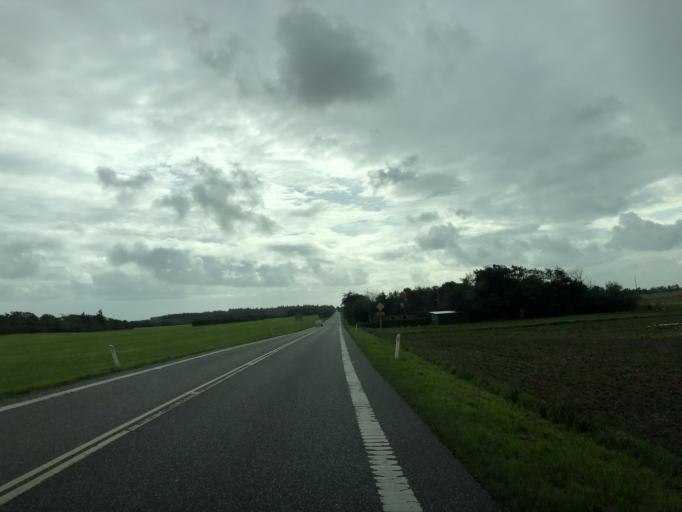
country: DK
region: North Denmark
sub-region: Thisted Kommune
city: Hurup
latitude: 56.7265
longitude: 8.4271
